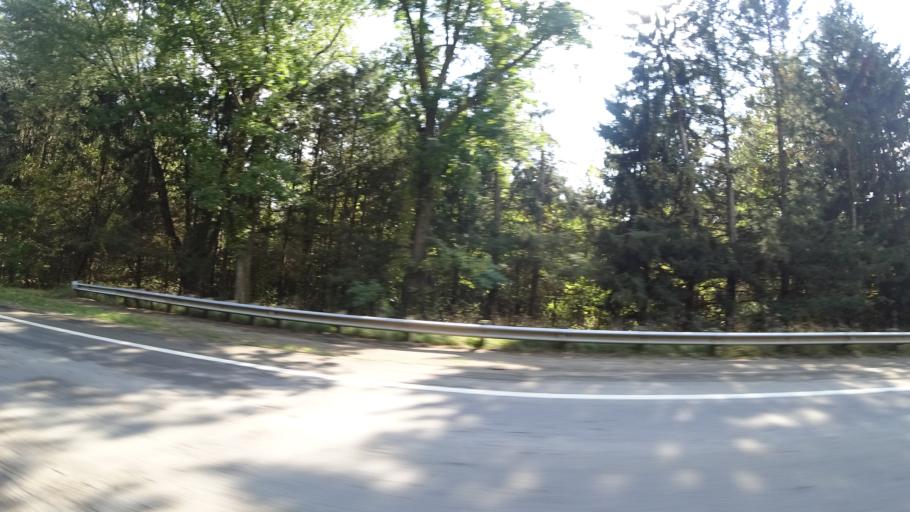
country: US
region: Michigan
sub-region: Saint Joseph County
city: Colon
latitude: 42.0102
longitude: -85.3875
